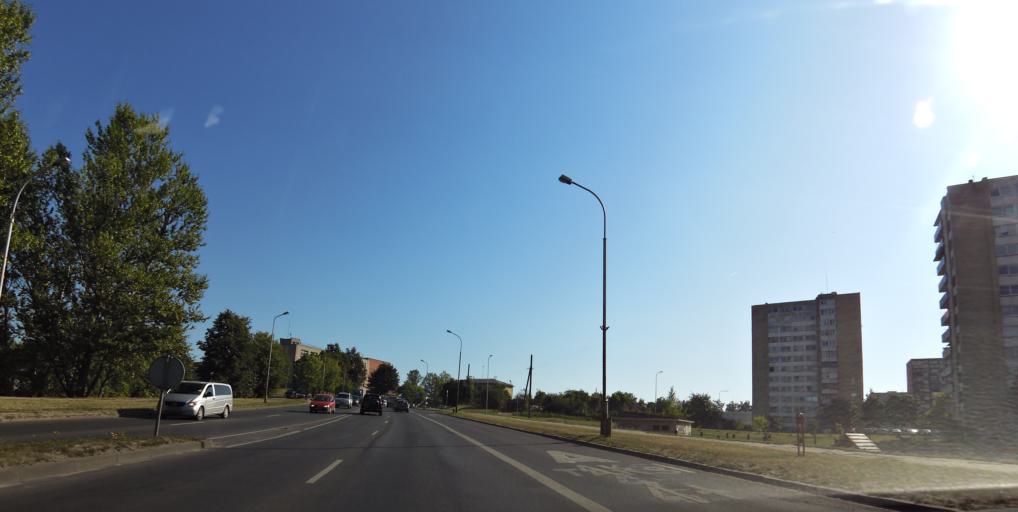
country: LT
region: Vilnius County
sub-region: Vilnius
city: Vilnius
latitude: 54.7138
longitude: 25.2822
